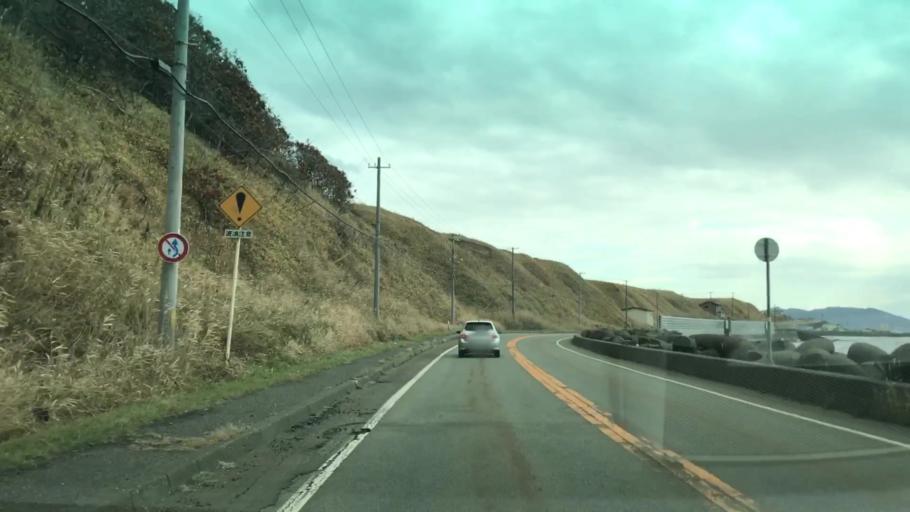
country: JP
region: Hokkaido
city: Shizunai-furukawacho
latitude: 42.0507
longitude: 143.0942
